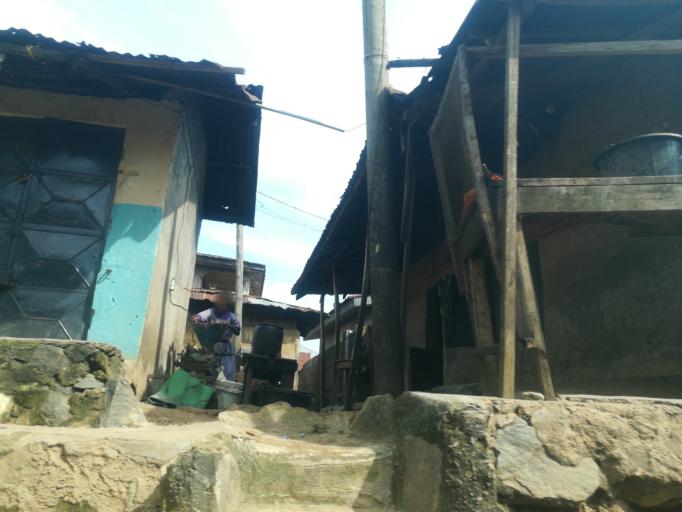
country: NG
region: Oyo
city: Ibadan
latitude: 7.3845
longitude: 3.8281
